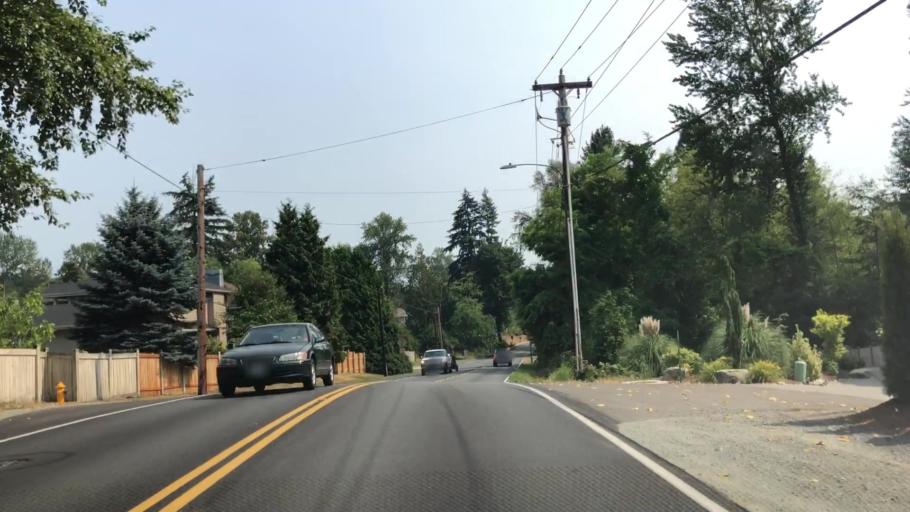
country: US
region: Washington
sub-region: Snohomish County
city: Brier
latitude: 47.7939
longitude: -122.2576
